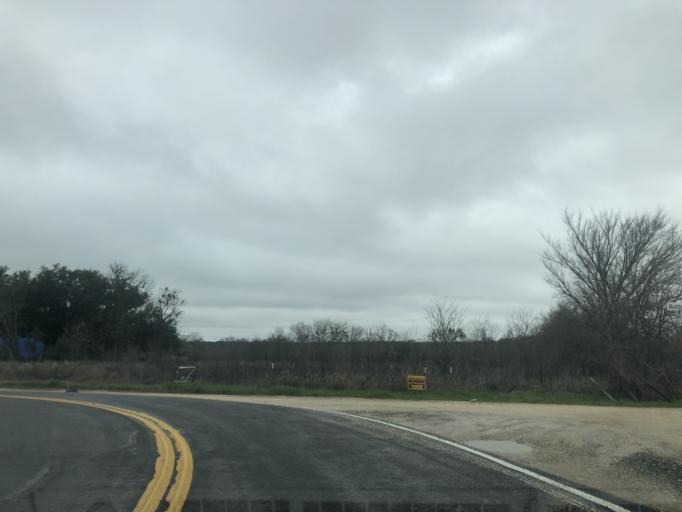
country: US
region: Texas
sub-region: Williamson County
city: Georgetown
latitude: 30.6500
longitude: -97.5830
